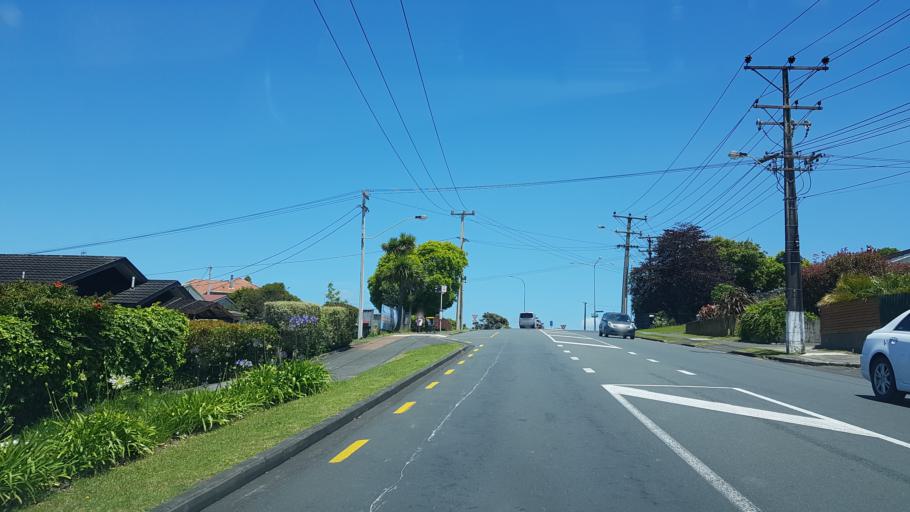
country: NZ
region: Auckland
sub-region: Auckland
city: North Shore
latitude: -36.7919
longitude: 174.7252
